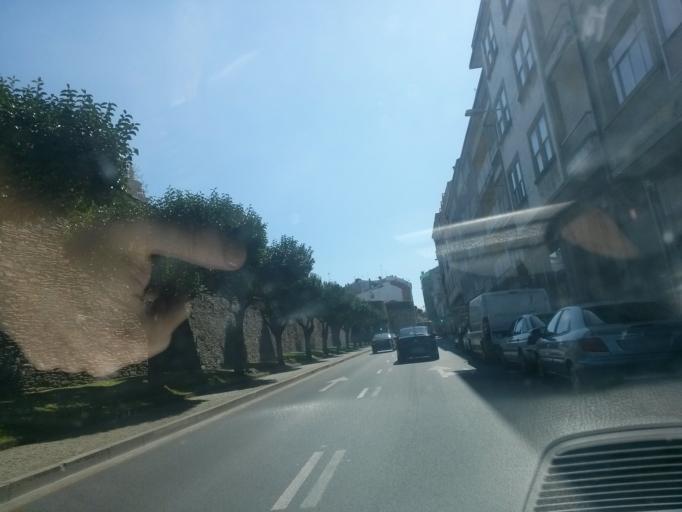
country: ES
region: Galicia
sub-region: Provincia de Lugo
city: Lugo
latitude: 43.0097
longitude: -7.5603
